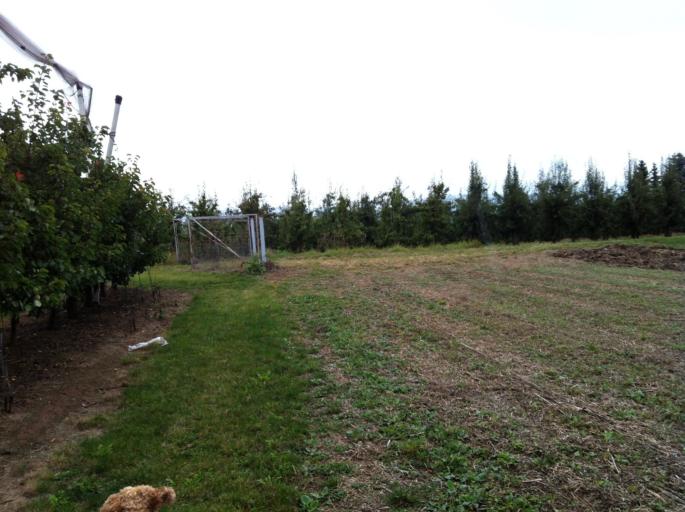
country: DE
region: Rheinland-Pfalz
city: Budenheim
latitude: 49.9787
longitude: 8.1809
